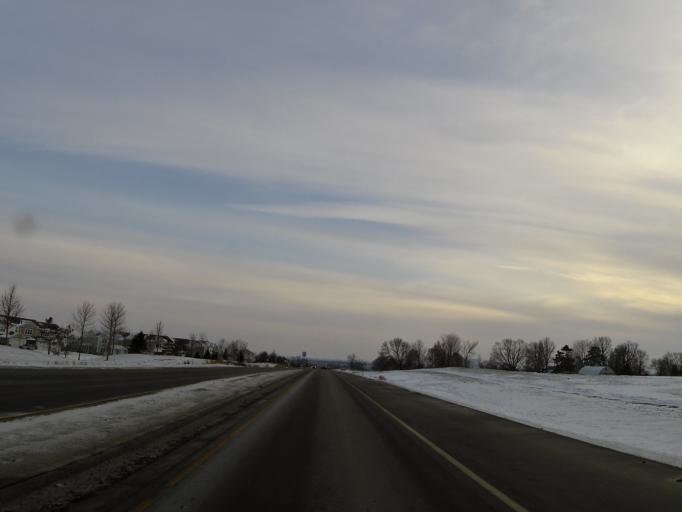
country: US
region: Minnesota
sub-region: Carver County
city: Carver
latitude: 44.7685
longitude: -93.6428
